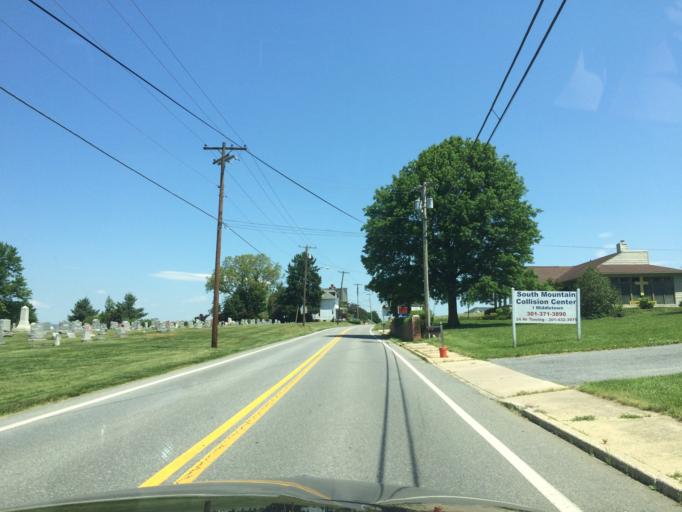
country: US
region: Maryland
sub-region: Frederick County
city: Middletown
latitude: 39.4455
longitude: -77.5448
